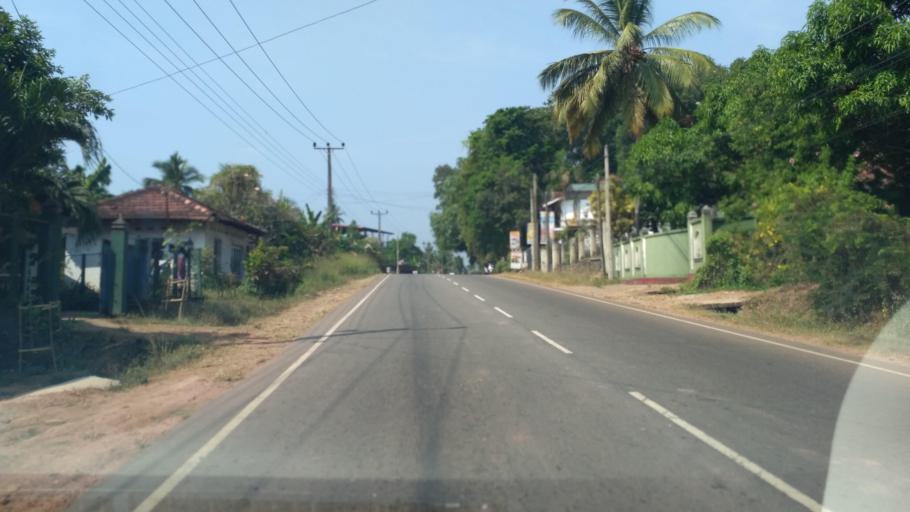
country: LK
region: North Western
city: Kuliyapitiya
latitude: 7.3341
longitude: 80.0083
